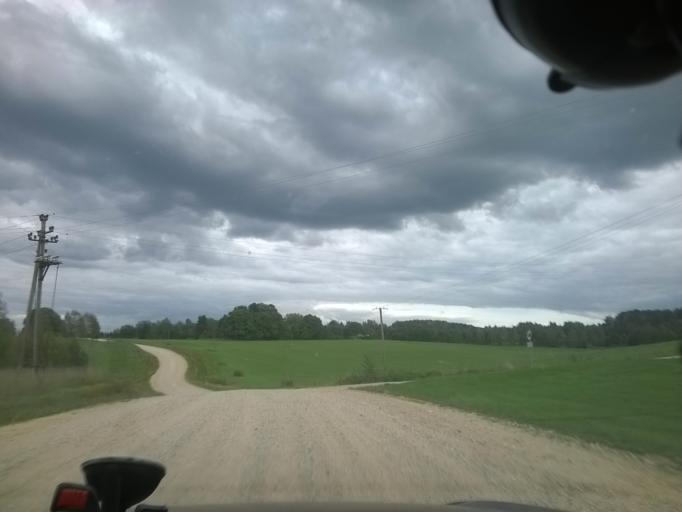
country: EE
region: Vorumaa
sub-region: Voru linn
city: Voru
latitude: 57.8112
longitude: 27.1680
